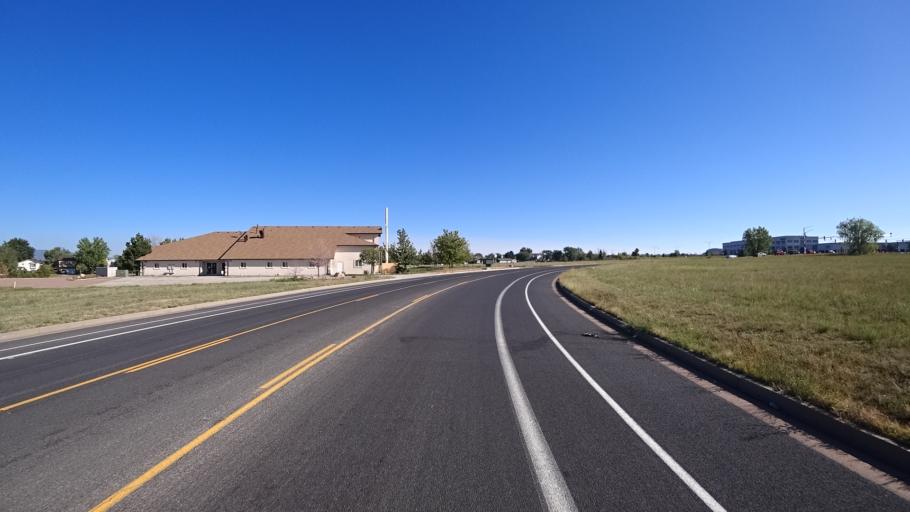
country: US
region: Colorado
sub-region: El Paso County
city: Cimarron Hills
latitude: 38.8158
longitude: -104.7320
